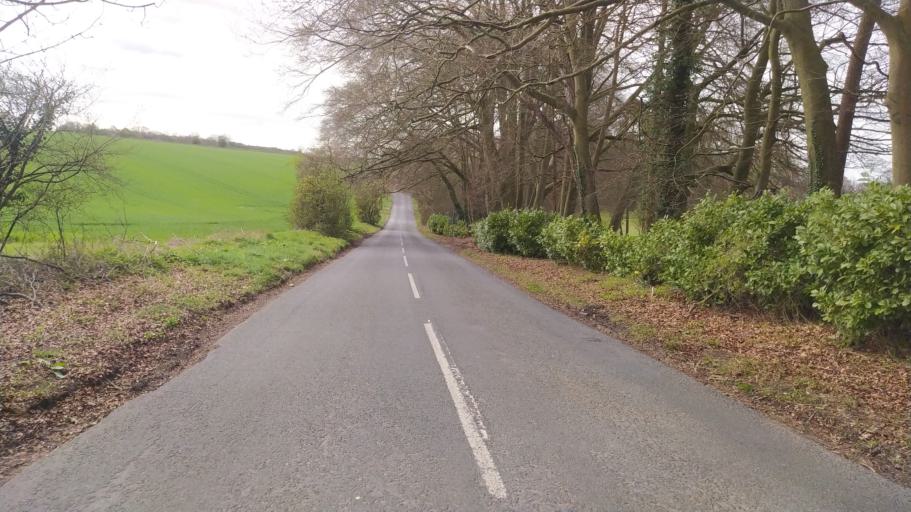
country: GB
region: England
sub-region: Hampshire
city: Bishops Waltham
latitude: 50.9954
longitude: -1.2057
